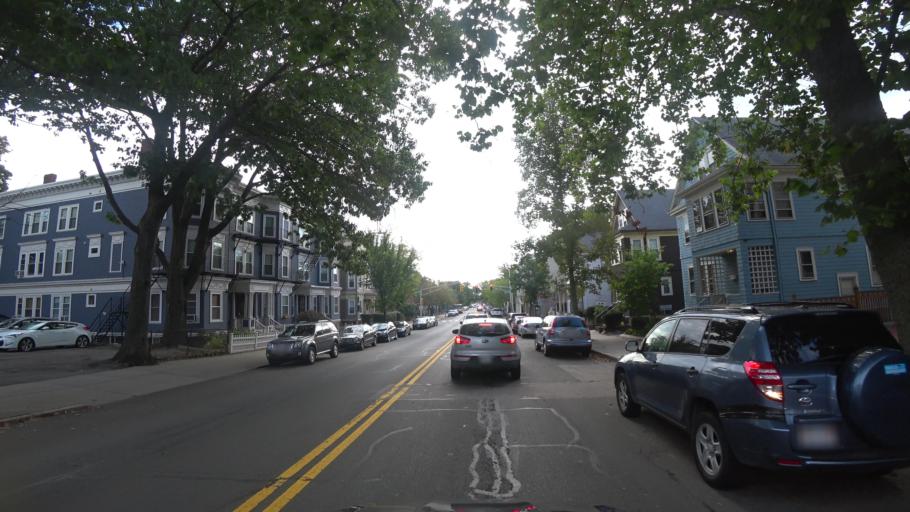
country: US
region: Massachusetts
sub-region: Middlesex County
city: Cambridge
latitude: 42.3711
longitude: -71.1056
